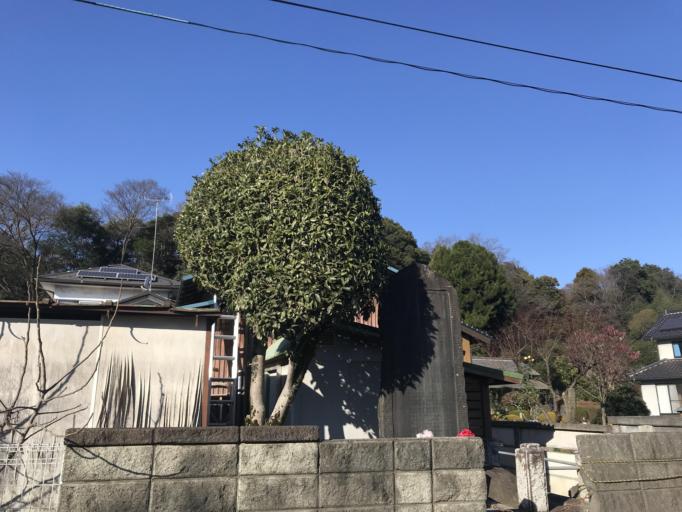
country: JP
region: Tochigi
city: Oyama
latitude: 36.2109
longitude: 139.8230
